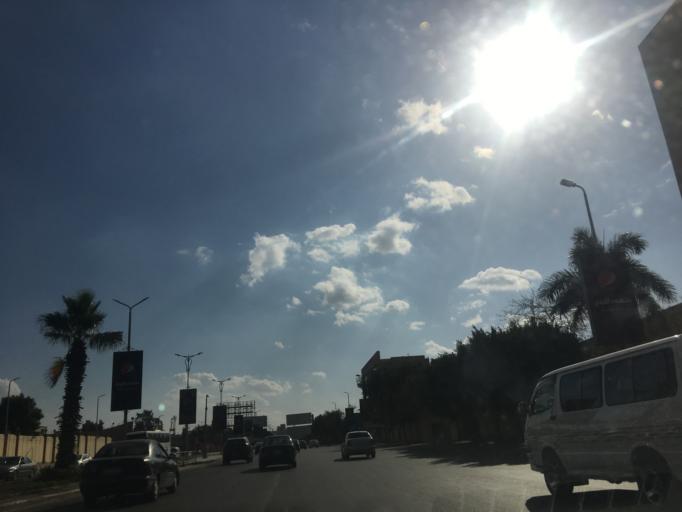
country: EG
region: Muhafazat al Qahirah
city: Cairo
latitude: 30.0526
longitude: 31.3073
